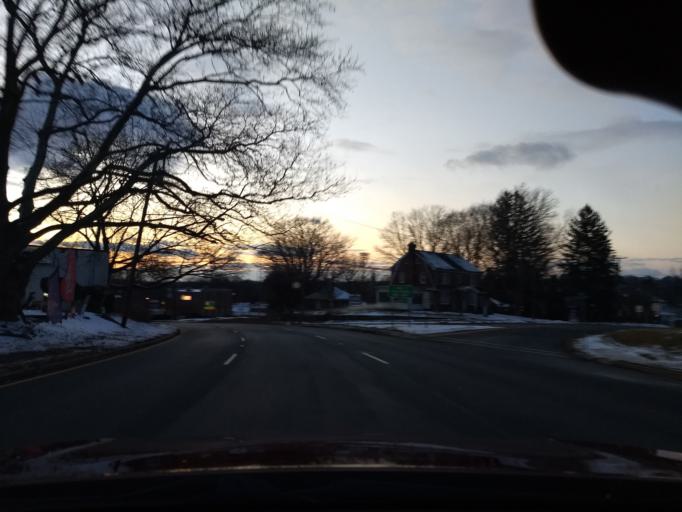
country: US
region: New Jersey
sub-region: Warren County
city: Phillipsburg
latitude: 40.6967
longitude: -75.1867
